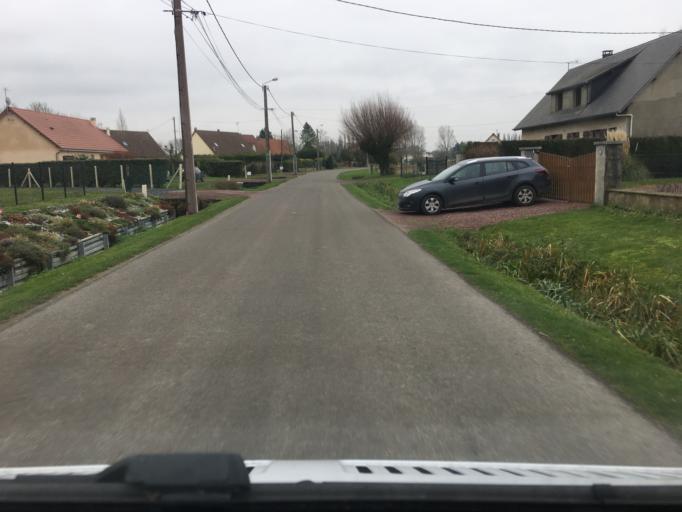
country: FR
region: Picardie
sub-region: Departement de la Somme
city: Pende
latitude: 50.1694
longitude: 1.5500
